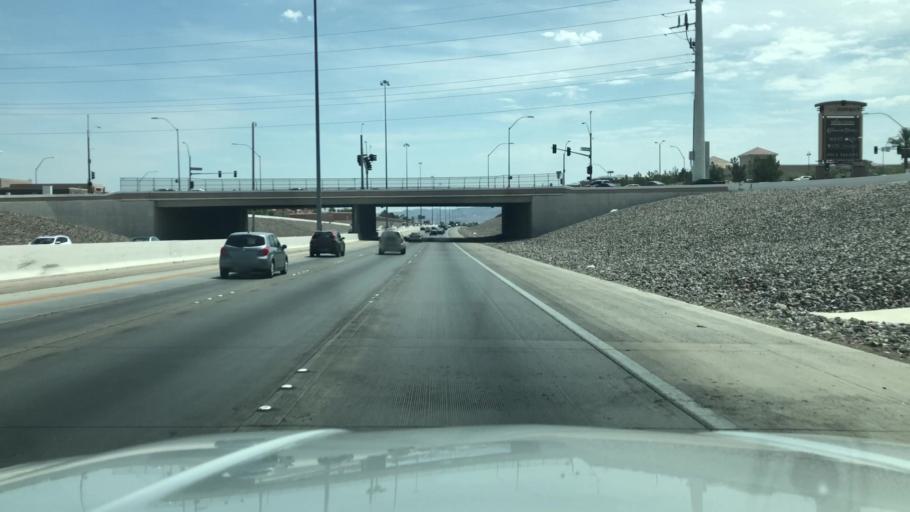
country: US
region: Nevada
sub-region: Clark County
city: Whitney
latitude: 36.0242
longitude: -115.0864
